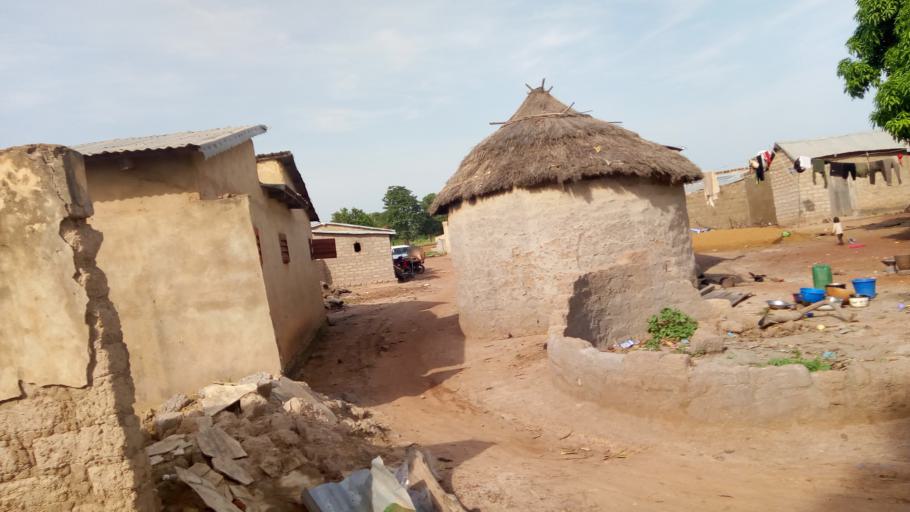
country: ML
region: Koulikoro
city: Kangaba
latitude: 11.6781
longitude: -8.7121
